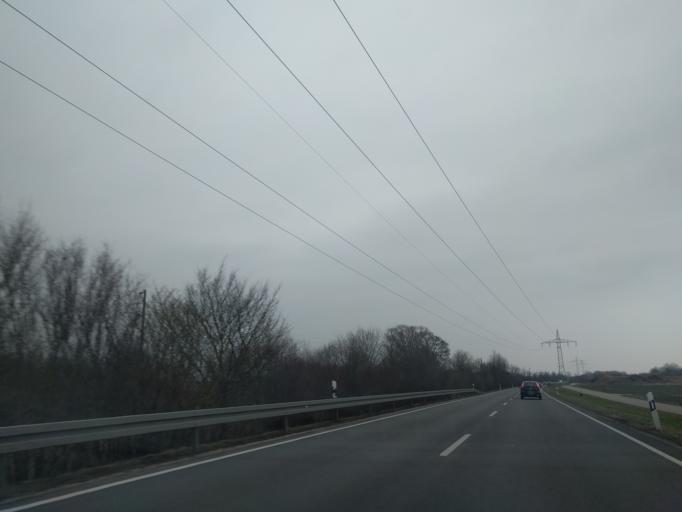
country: DE
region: Bavaria
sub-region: Swabia
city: Oberndorf
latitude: 48.6934
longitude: 10.8483
